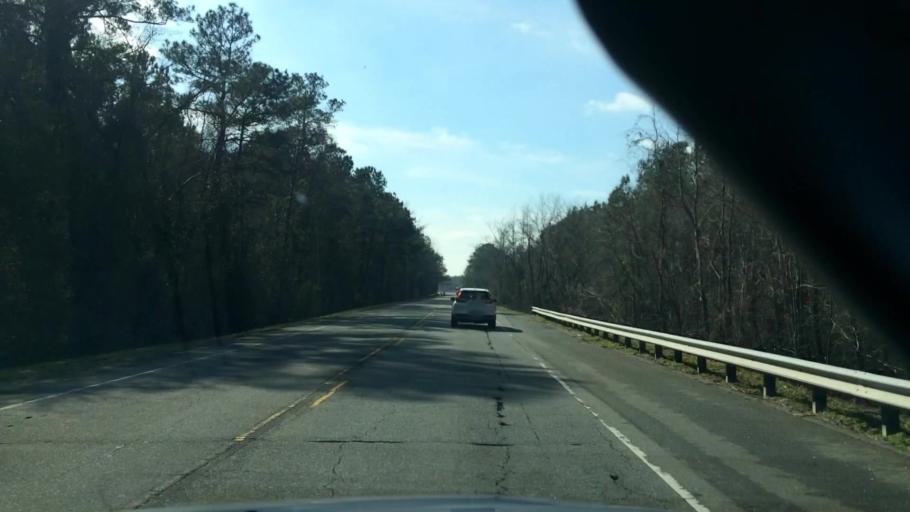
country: US
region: North Carolina
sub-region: Duplin County
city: Beulaville
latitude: 34.8294
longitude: -77.8349
